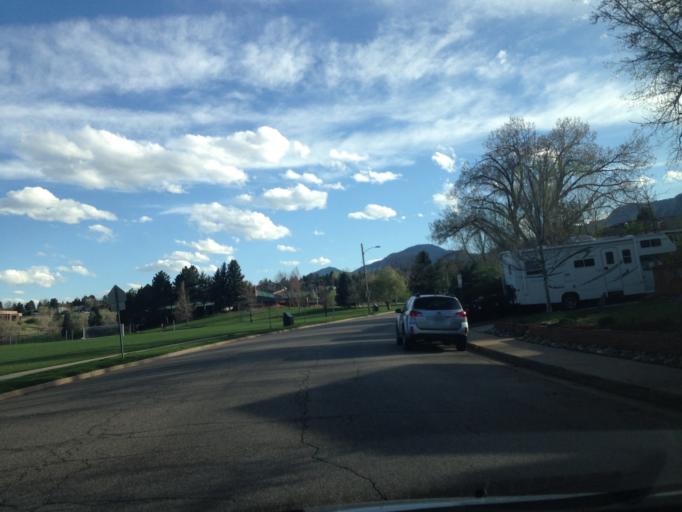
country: US
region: Colorado
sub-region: Boulder County
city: Boulder
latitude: 39.9767
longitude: -105.2481
